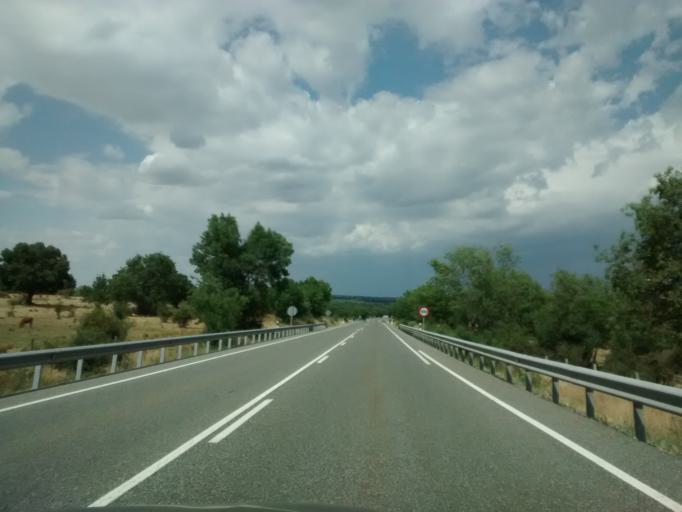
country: ES
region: Castille and Leon
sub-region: Provincia de Segovia
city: Gallegos
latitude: 41.0846
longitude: -3.7932
